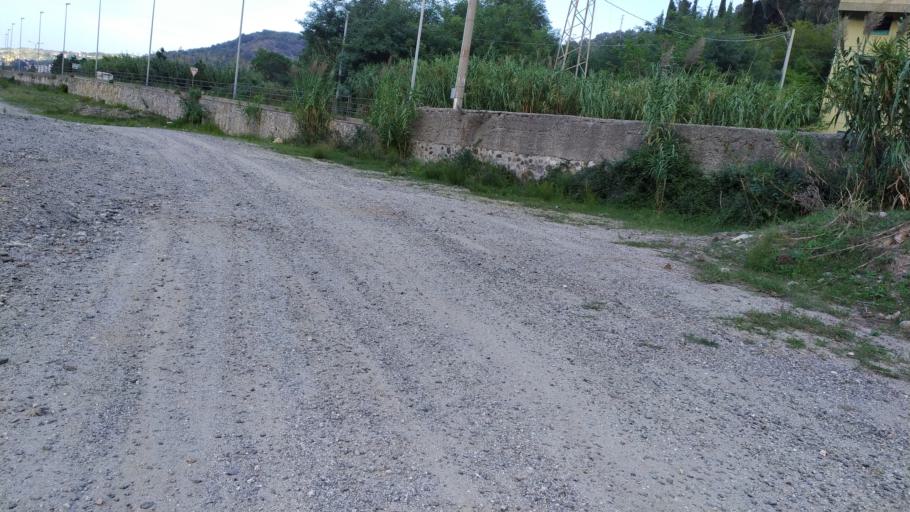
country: IT
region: Sicily
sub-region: Messina
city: Saponara
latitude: 38.1968
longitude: 15.4298
